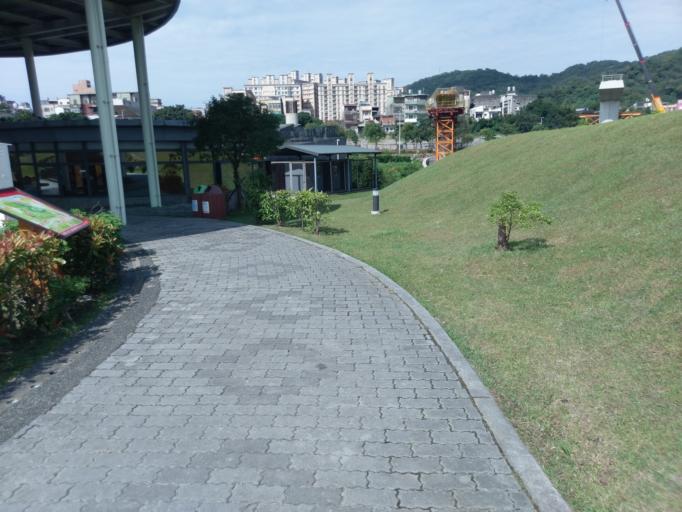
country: TW
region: Taiwan
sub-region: Taoyuan
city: Taoyuan
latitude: 24.9533
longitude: 121.3586
